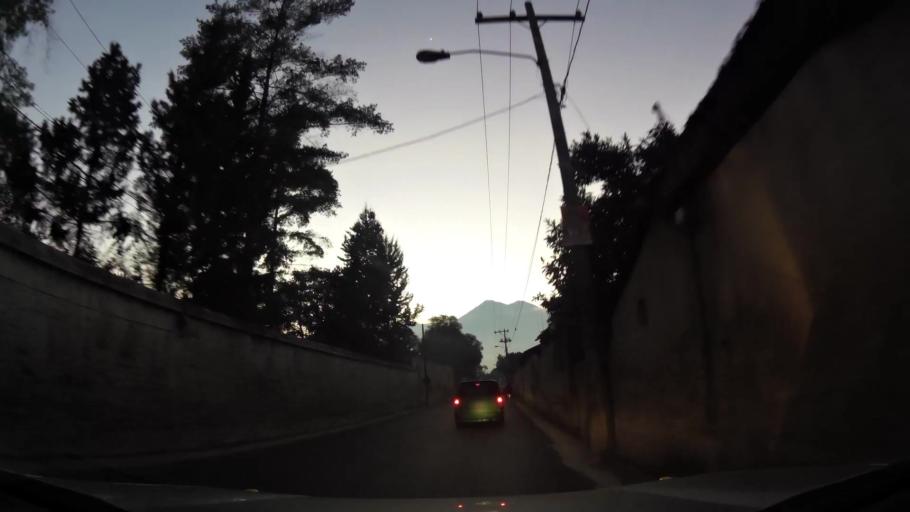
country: GT
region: Sacatepequez
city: Ciudad Vieja
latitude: 14.5280
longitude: -90.7594
